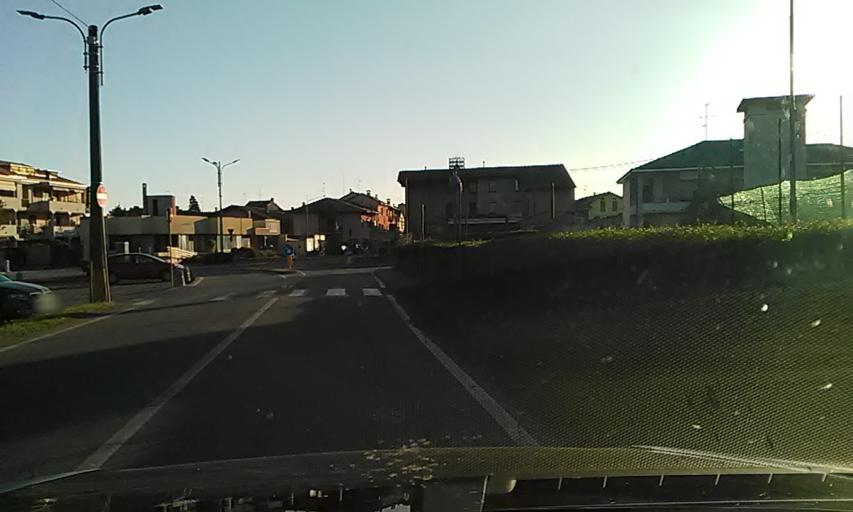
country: IT
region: Piedmont
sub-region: Provincia di Novara
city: Carpignano Sesia
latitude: 45.5366
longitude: 8.4222
